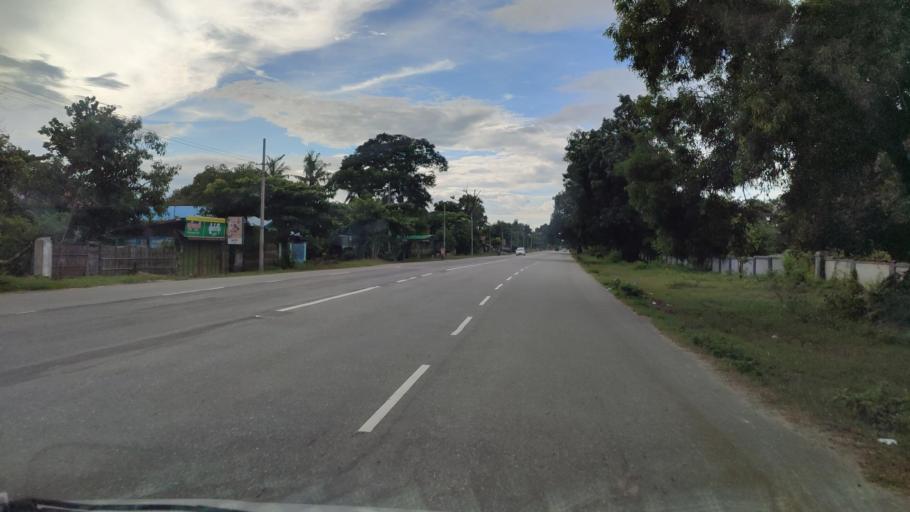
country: MM
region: Bago
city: Taungoo
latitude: 19.0223
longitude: 96.3785
